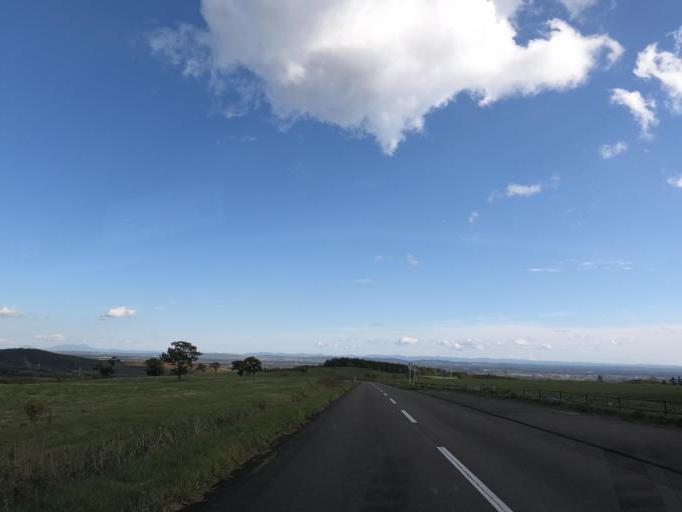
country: JP
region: Hokkaido
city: Otofuke
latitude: 43.2780
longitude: 143.2275
